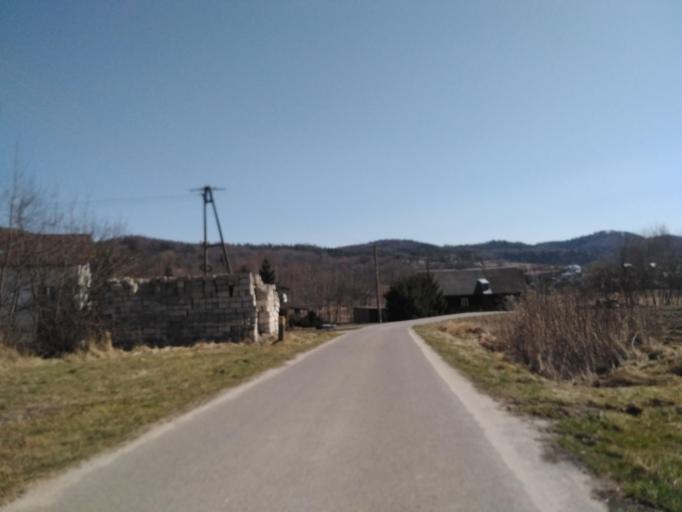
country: PL
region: Subcarpathian Voivodeship
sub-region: Powiat brzozowski
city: Jasienica Rosielna
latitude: 49.7626
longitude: 21.9568
